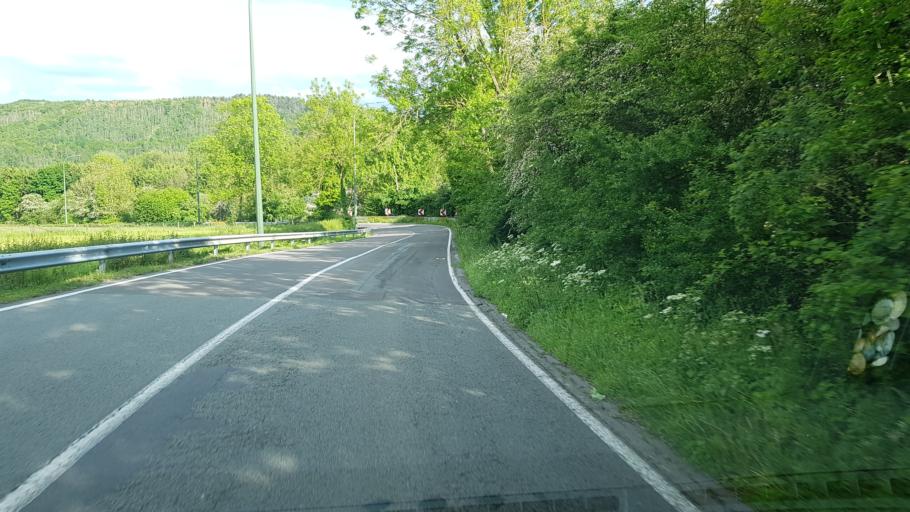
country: BE
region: Wallonia
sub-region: Province de Liege
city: Trooz
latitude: 50.5440
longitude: 5.6835
